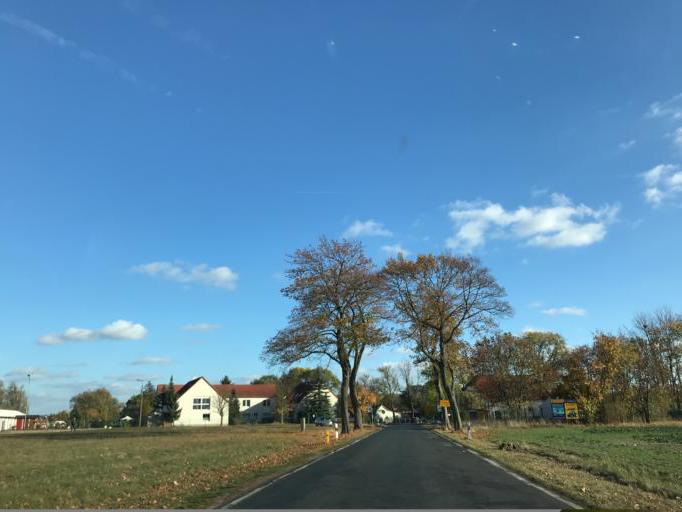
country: DE
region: Brandenburg
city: Schonermark
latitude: 53.0074
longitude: 13.1118
